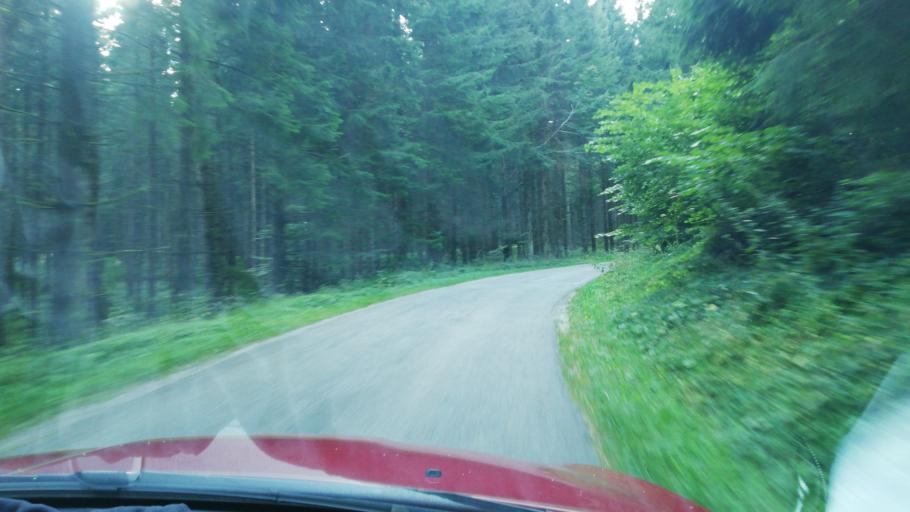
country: AT
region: Lower Austria
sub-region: Politischer Bezirk Zwettl
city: Langschlag
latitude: 48.4710
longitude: 14.8253
